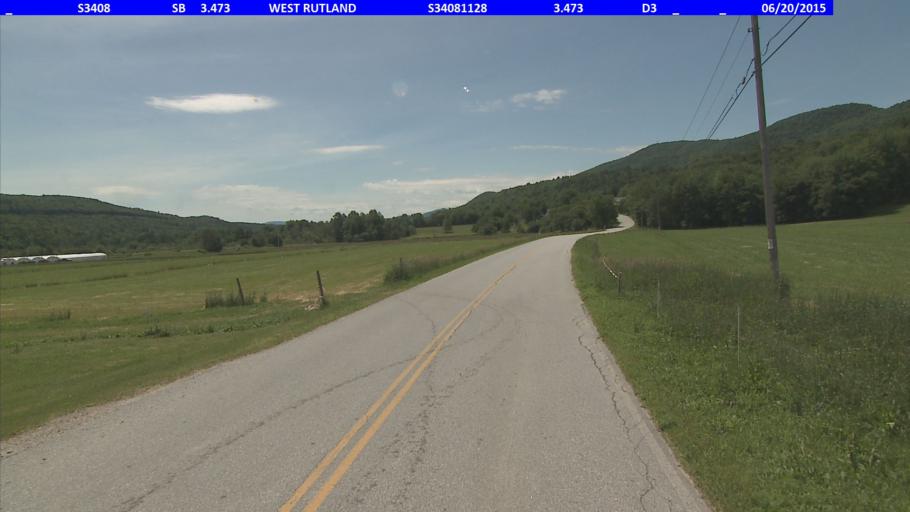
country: US
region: Vermont
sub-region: Rutland County
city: West Rutland
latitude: 43.6588
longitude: -73.0734
